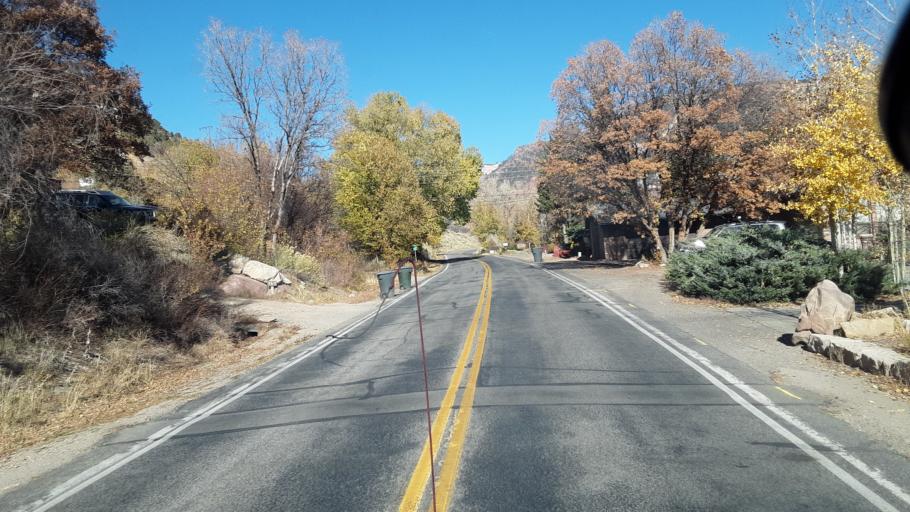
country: US
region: Colorado
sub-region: La Plata County
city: Durango
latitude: 37.3115
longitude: -107.8544
